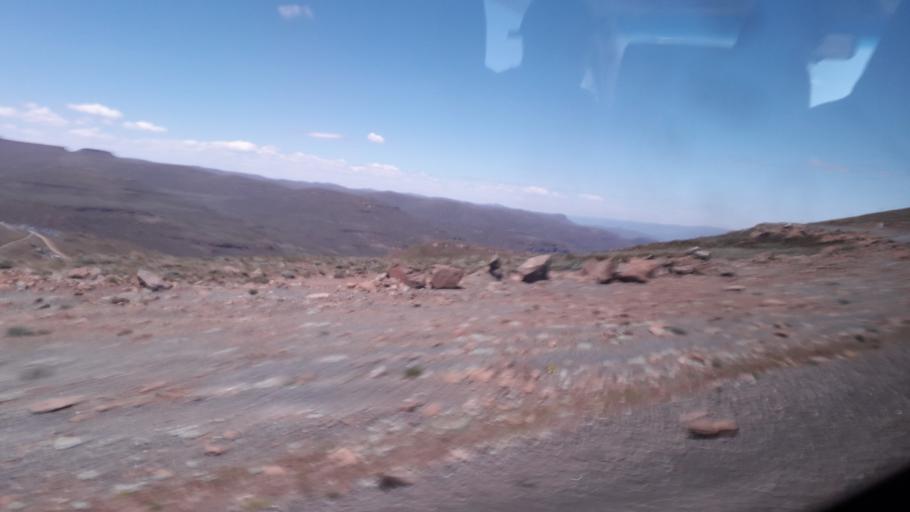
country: ZA
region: Orange Free State
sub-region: Thabo Mofutsanyana District Municipality
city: Phuthaditjhaba
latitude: -28.8092
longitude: 28.7264
